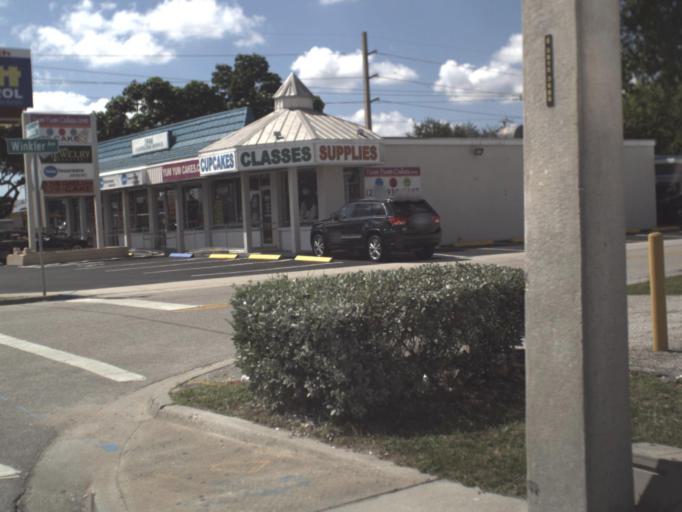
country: US
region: Florida
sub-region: Lee County
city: Pine Manor
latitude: 26.6049
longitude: -81.8720
